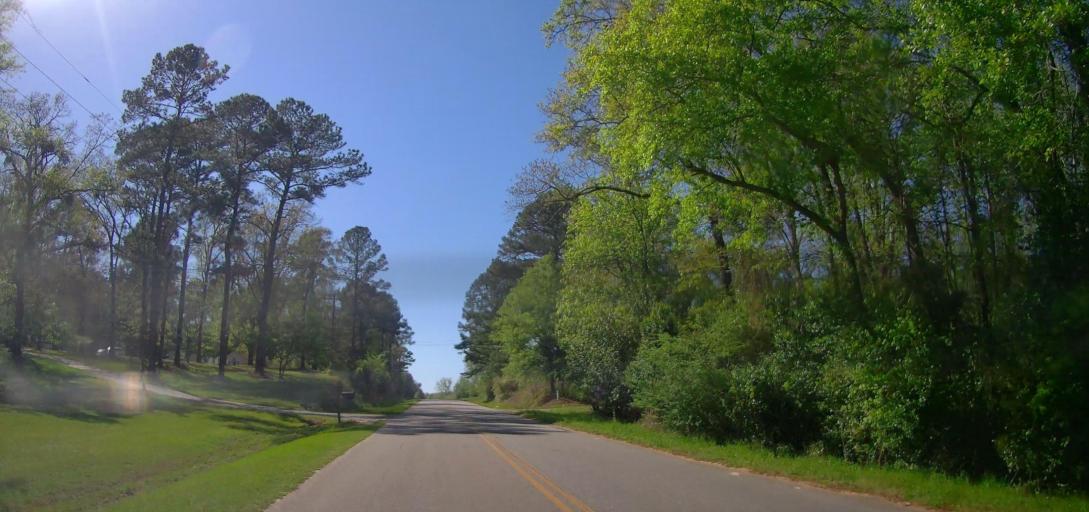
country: US
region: Georgia
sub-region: Pulaski County
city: Hawkinsville
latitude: 32.2374
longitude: -83.5053
